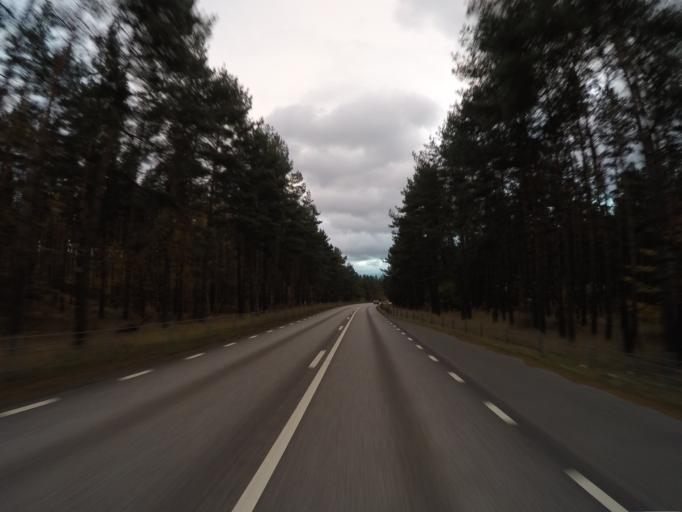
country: SE
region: Skane
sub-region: Kristianstads Kommun
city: Degeberga
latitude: 55.9085
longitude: 14.0730
